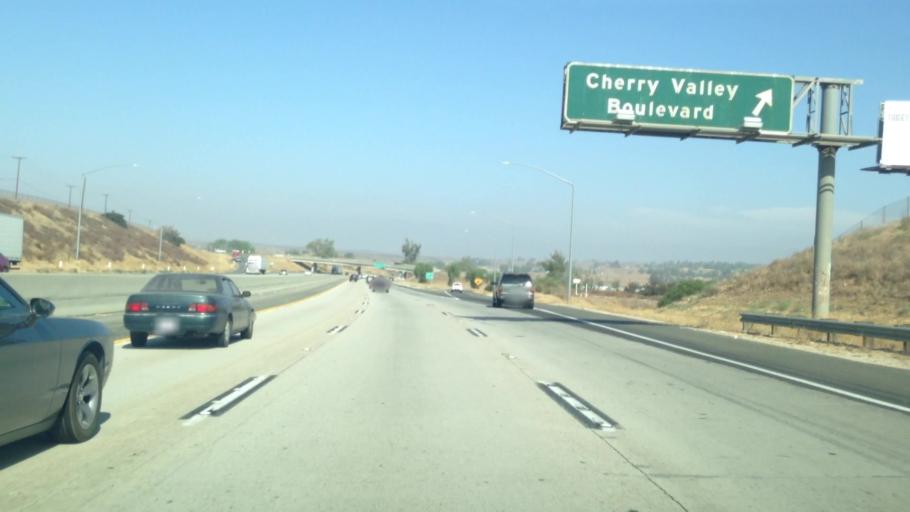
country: US
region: California
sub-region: Riverside County
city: Calimesa
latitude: 33.9660
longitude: -117.0313
